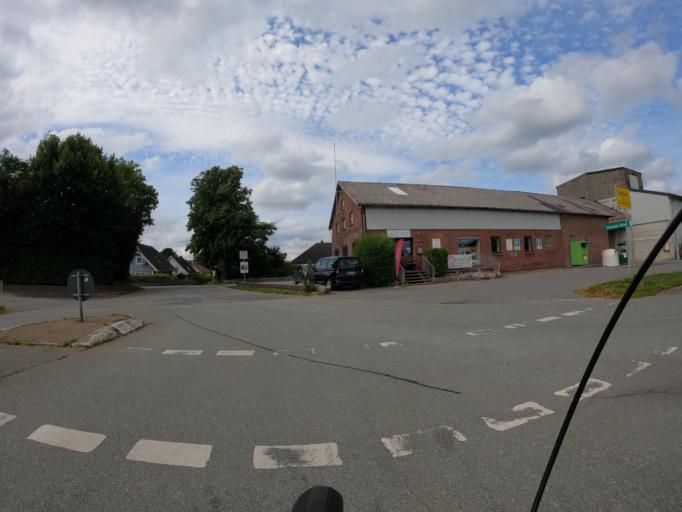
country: DE
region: Schleswig-Holstein
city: Steinberg
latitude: 54.7547
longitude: 9.7859
